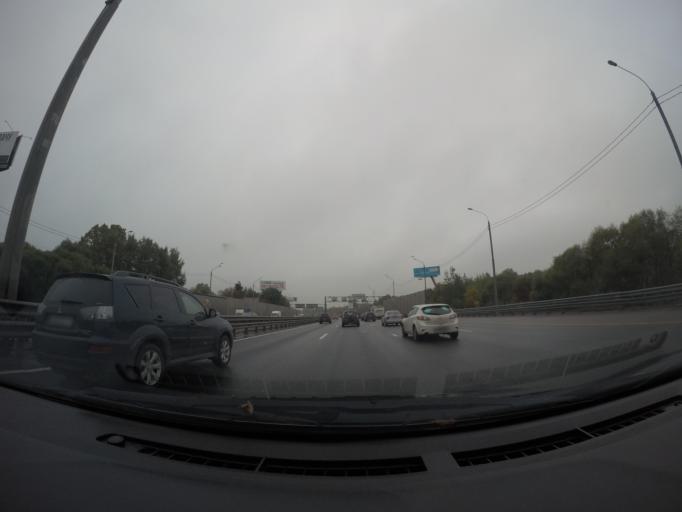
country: RU
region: Moskovskaya
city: Arkhangel'skoye
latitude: 55.7964
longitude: 37.2707
